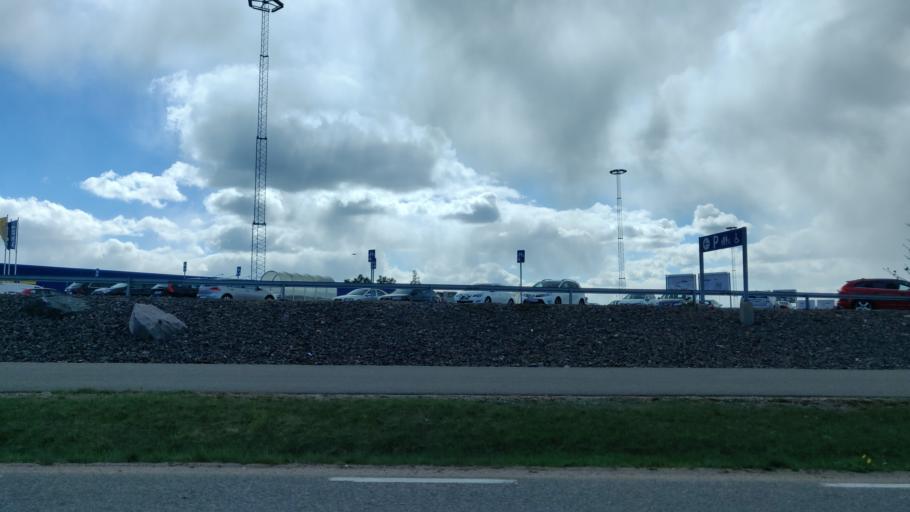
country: SE
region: Vaermland
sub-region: Hammaro Kommun
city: Skoghall
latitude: 59.3803
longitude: 13.4200
